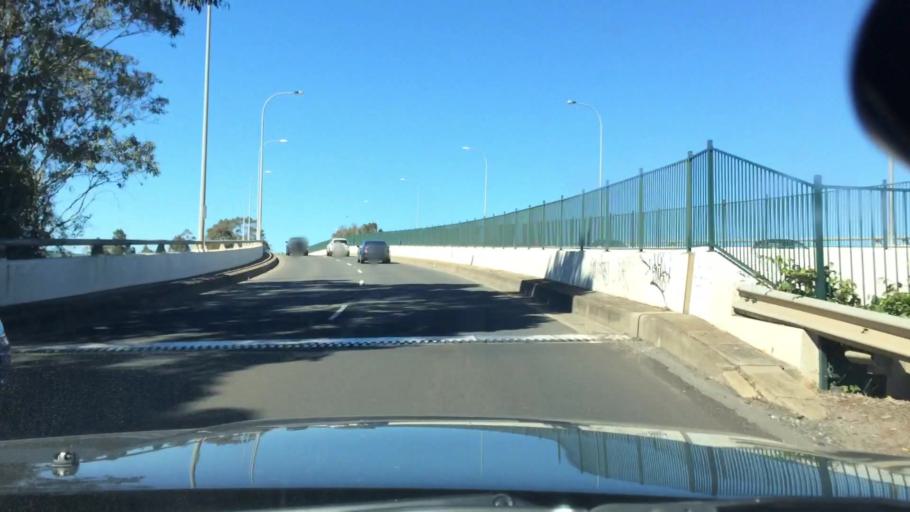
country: AU
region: New South Wales
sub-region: Campbelltown Municipality
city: Campbelltown
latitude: -34.0706
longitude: 150.8001
